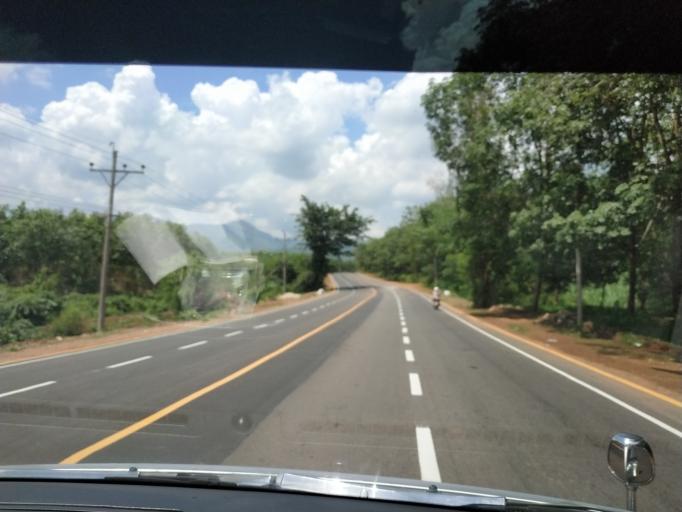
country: MM
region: Mon
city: Kyaikto
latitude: 17.3891
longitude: 97.0607
